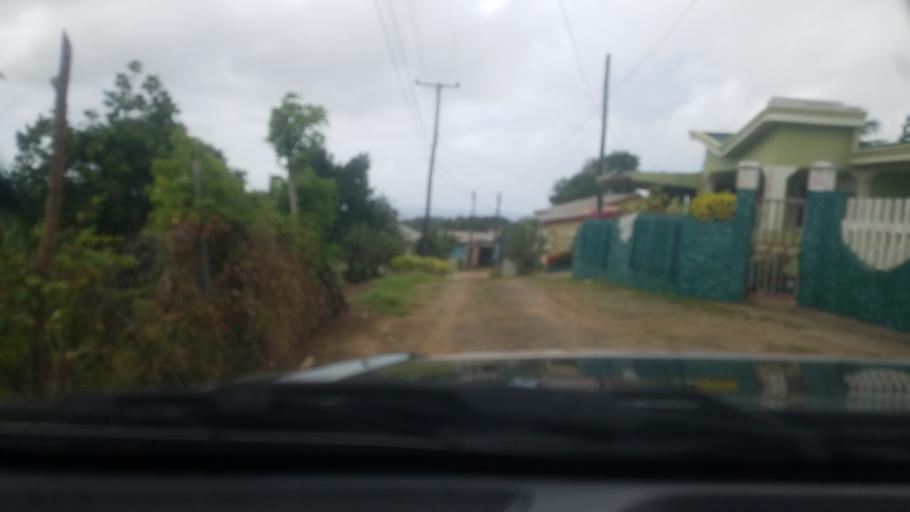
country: LC
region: Micoud Quarter
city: Micoud
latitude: 13.8039
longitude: -60.9407
